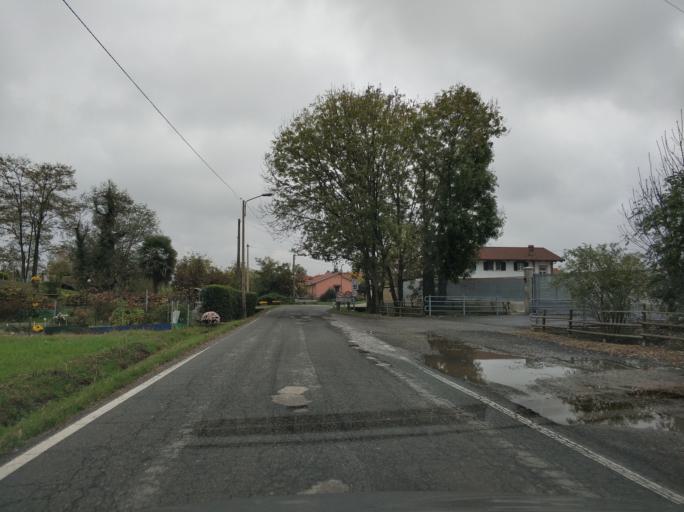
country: IT
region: Piedmont
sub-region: Provincia di Torino
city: Villanova Canavese
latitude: 45.2453
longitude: 7.5466
